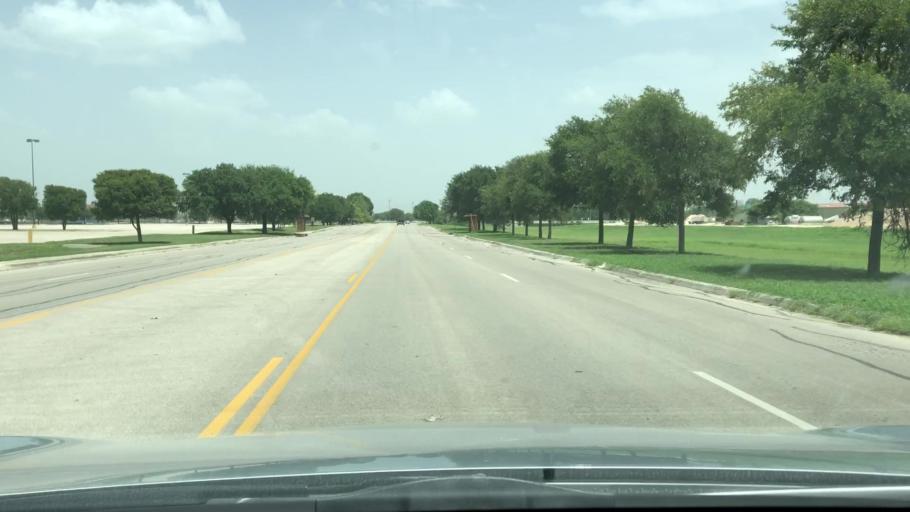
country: US
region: Texas
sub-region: Bexar County
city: Selma
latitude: 29.5829
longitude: -98.3189
